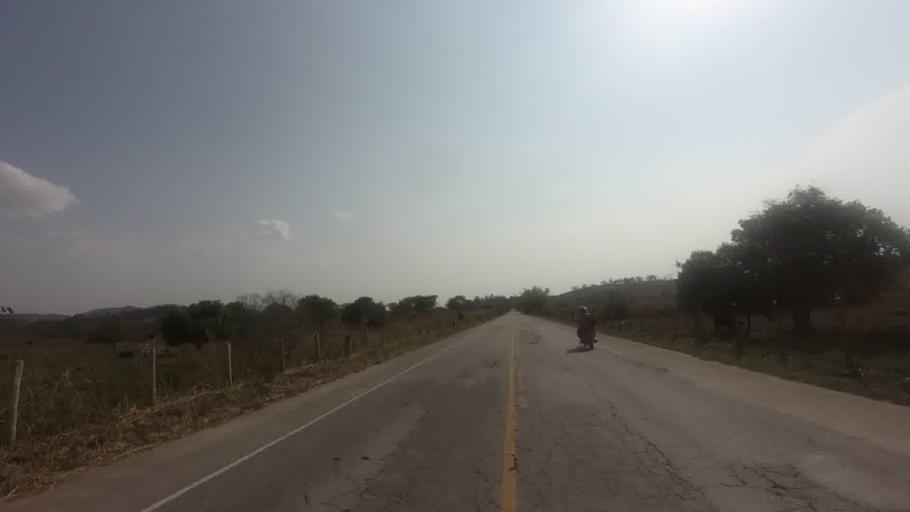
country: BR
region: Rio de Janeiro
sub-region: Bom Jesus Do Itabapoana
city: Bom Jesus do Itabapoana
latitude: -21.1466
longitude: -41.5833
